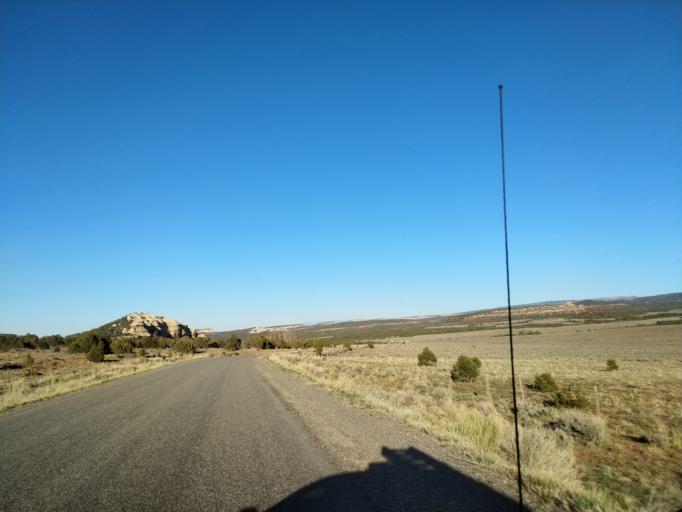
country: US
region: Colorado
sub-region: Mesa County
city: Loma
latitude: 38.9518
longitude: -108.9531
